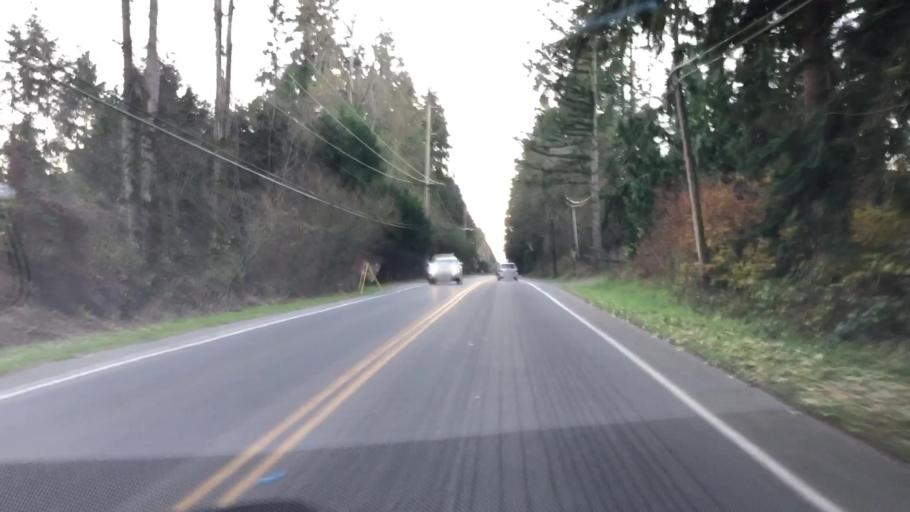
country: US
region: Washington
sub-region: King County
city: Yarrow Point
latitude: 47.6491
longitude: -122.1856
